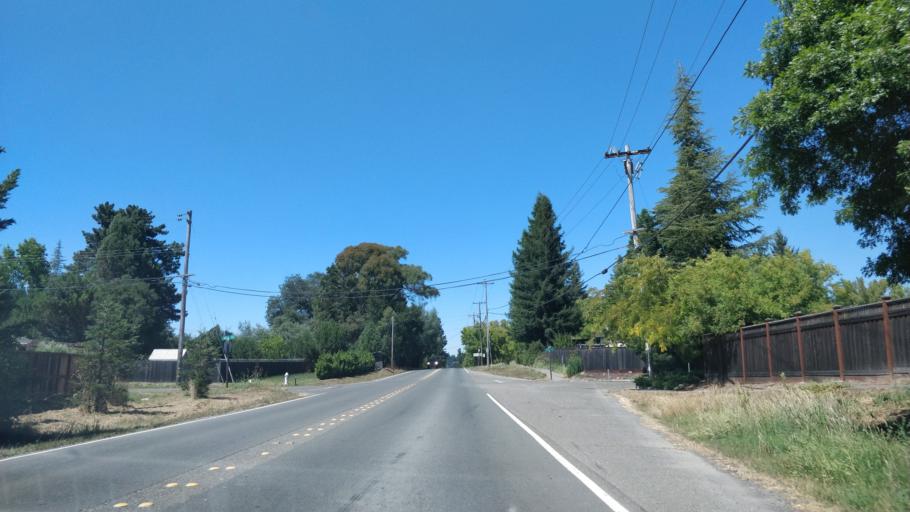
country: US
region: California
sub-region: Sonoma County
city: Forestville
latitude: 38.4777
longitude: -122.8948
